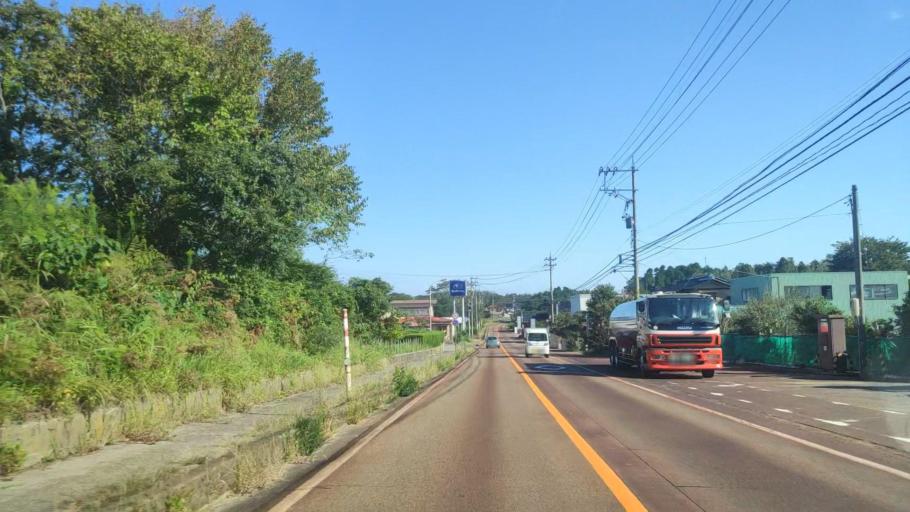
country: JP
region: Ishikawa
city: Hakui
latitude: 36.8727
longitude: 136.7733
